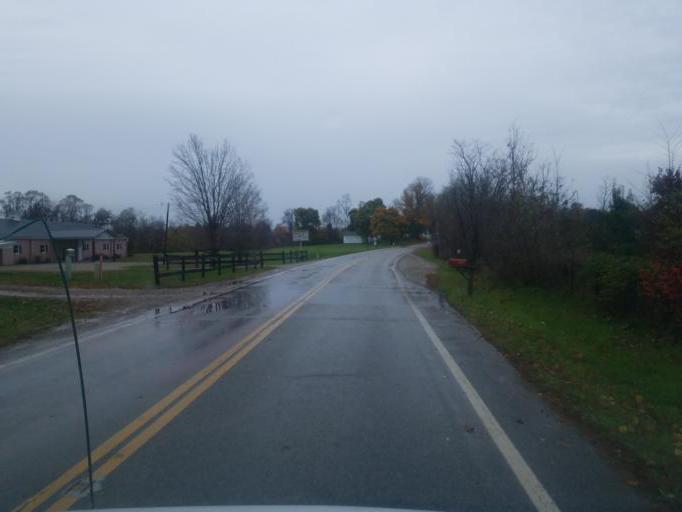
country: US
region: Ohio
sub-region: Morgan County
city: McConnelsville
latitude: 39.4841
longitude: -81.8683
